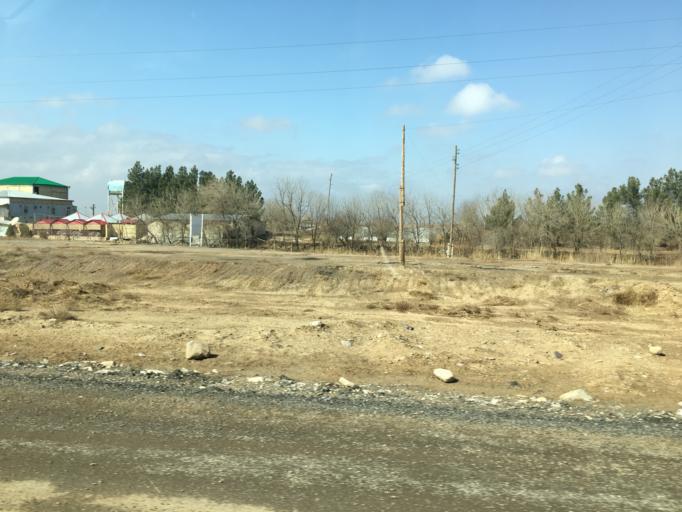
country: IR
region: Razavi Khorasan
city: Sarakhs
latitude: 37.2357
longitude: 61.2323
